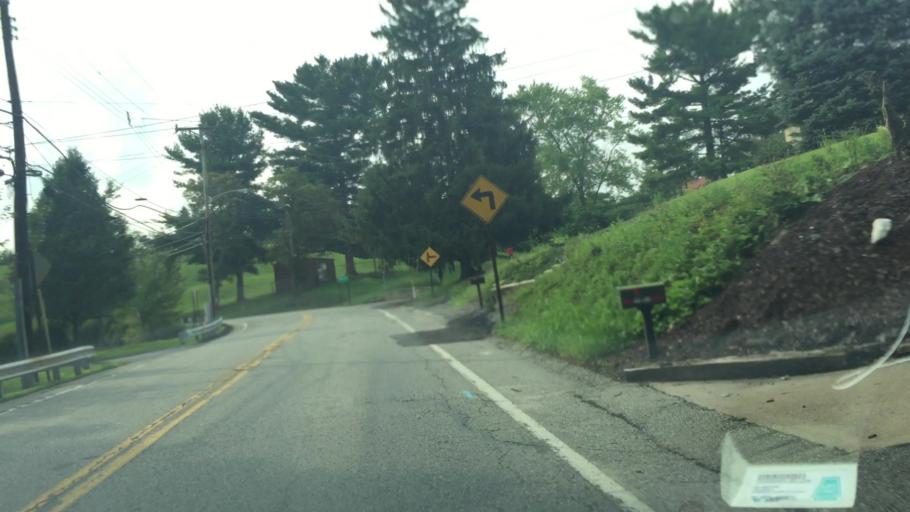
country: US
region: Pennsylvania
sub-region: Allegheny County
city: Bellevue
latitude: 40.5068
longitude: -80.0470
